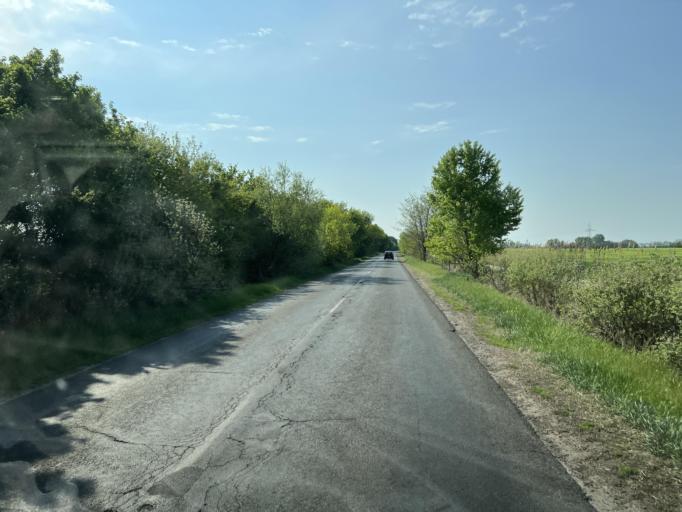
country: HU
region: Pest
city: Jaszkarajeno
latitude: 47.0802
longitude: 20.0418
